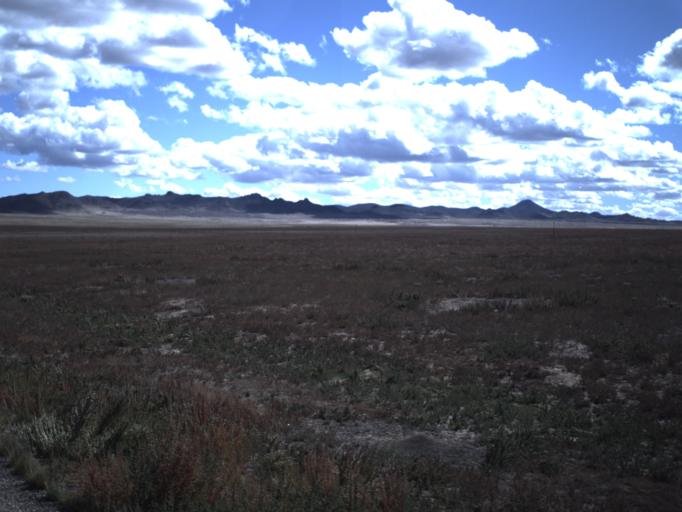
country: US
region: Utah
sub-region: Beaver County
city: Milford
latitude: 38.4615
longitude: -113.3794
